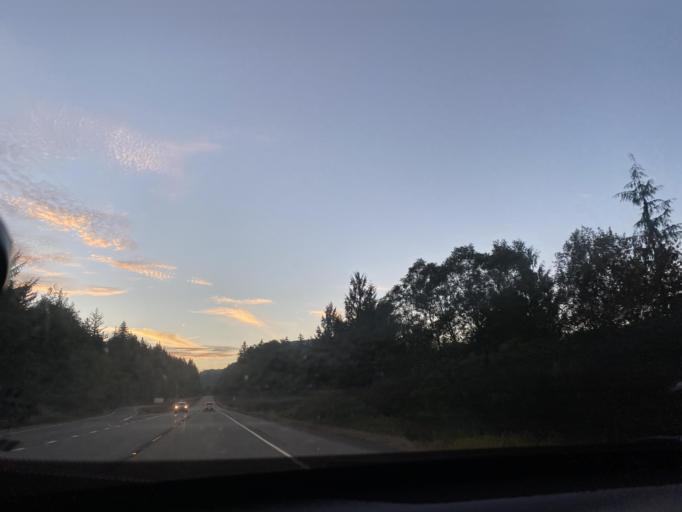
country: US
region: Washington
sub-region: Clallam County
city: Port Angeles
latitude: 48.0686
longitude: -123.6224
